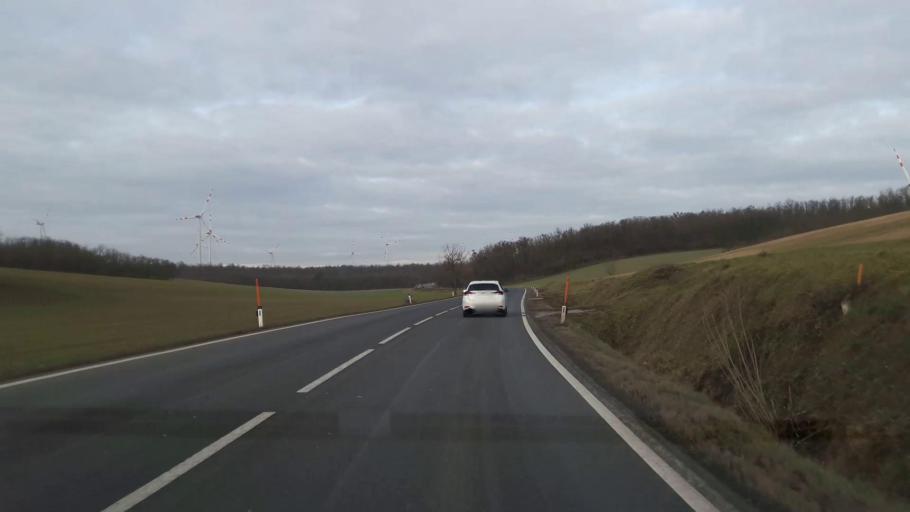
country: AT
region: Lower Austria
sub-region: Politischer Bezirk Mistelbach
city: Mistelbach
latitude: 48.5216
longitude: 16.6148
